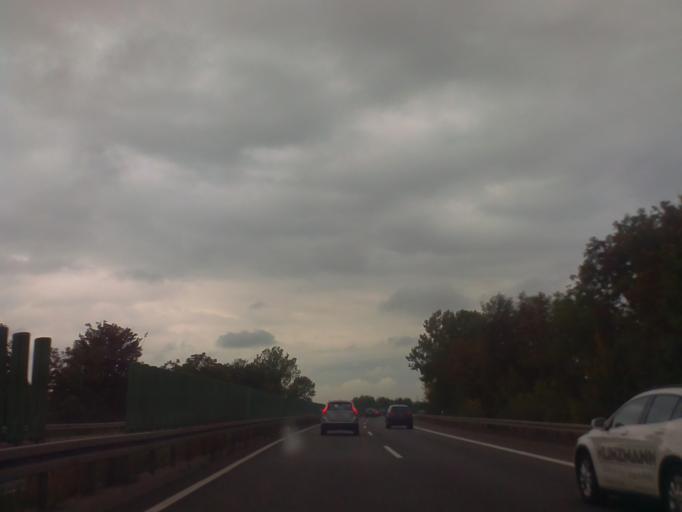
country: DE
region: Hesse
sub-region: Regierungsbezirk Darmstadt
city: Gelnhausen
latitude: 50.1909
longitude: 9.1662
